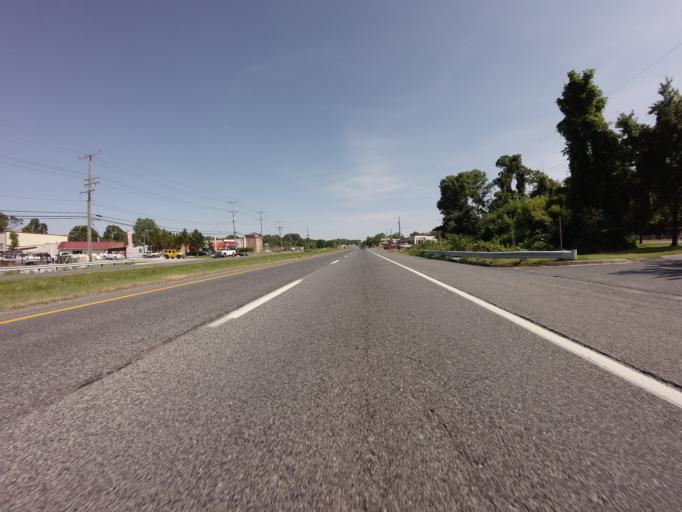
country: US
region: Maryland
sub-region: Baltimore County
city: Edgemere
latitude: 39.2633
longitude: -76.4655
